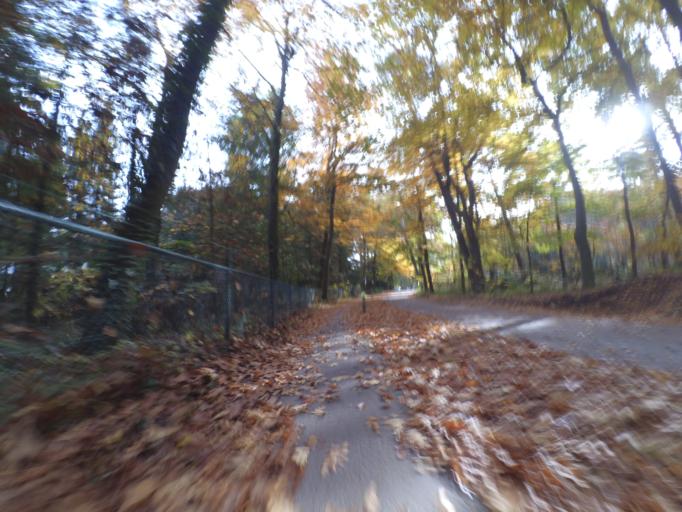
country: NL
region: Gelderland
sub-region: Gemeente Ede
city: Lunteren
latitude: 52.0868
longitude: 5.6347
